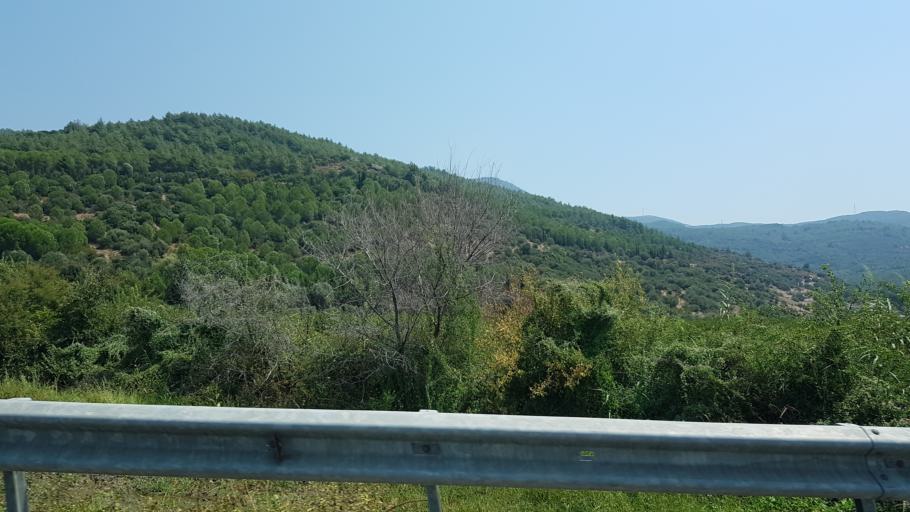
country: TR
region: Izmir
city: Belevi
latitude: 37.9929
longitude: 27.4137
